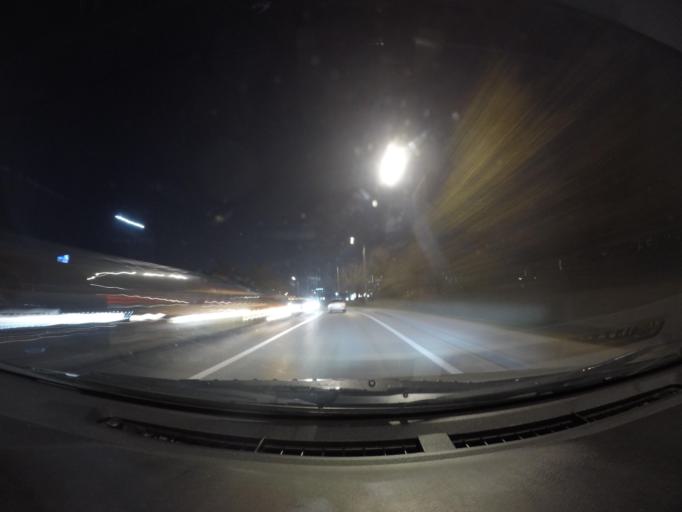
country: RU
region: Moscow
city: Khimki
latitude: 55.9170
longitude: 37.3932
